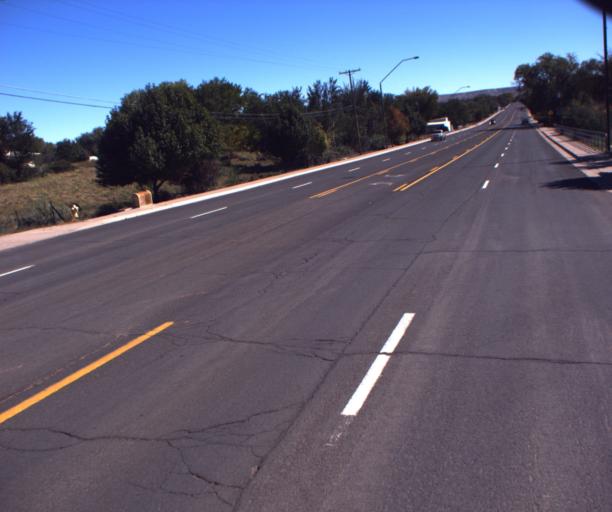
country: US
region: Arizona
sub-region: Apache County
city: Saint Johns
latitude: 34.5065
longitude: -109.3772
